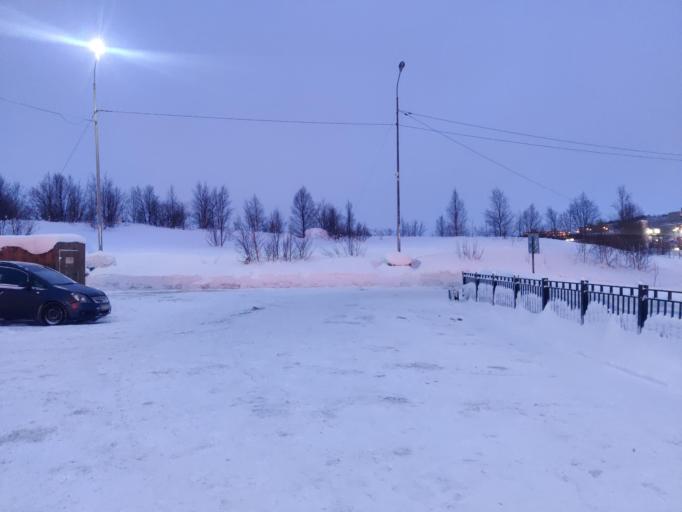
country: RU
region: Murmansk
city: Murmansk
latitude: 68.9876
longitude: 33.0880
